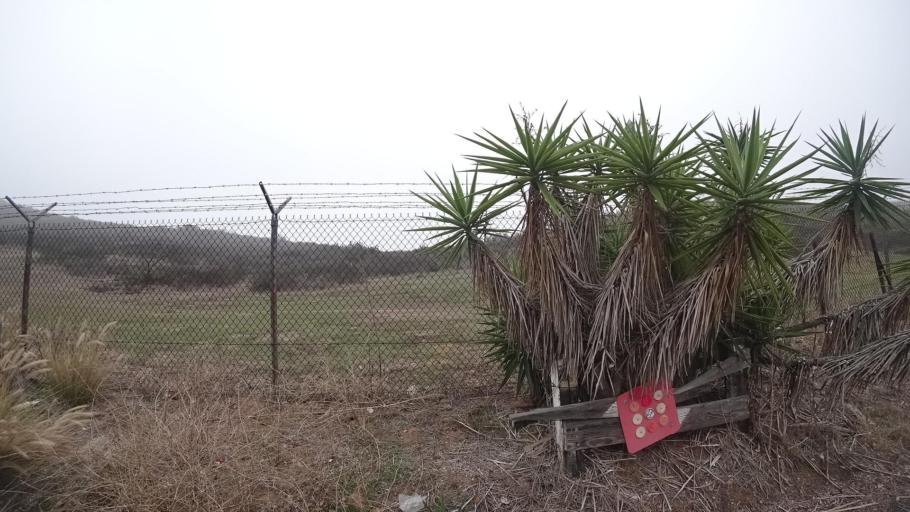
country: US
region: California
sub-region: San Diego County
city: Rancho San Diego
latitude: 32.7306
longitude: -116.9551
